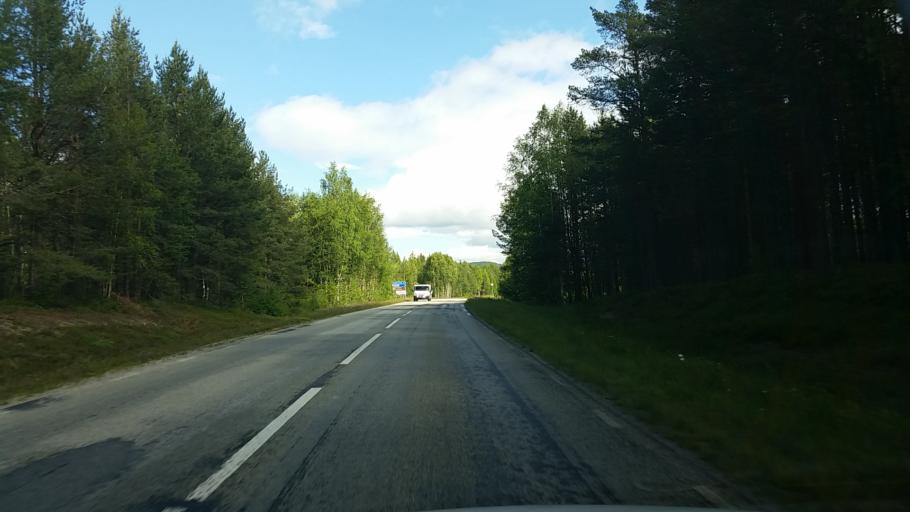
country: SE
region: Jaemtland
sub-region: Harjedalens Kommun
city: Sveg
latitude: 62.4126
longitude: 13.6714
